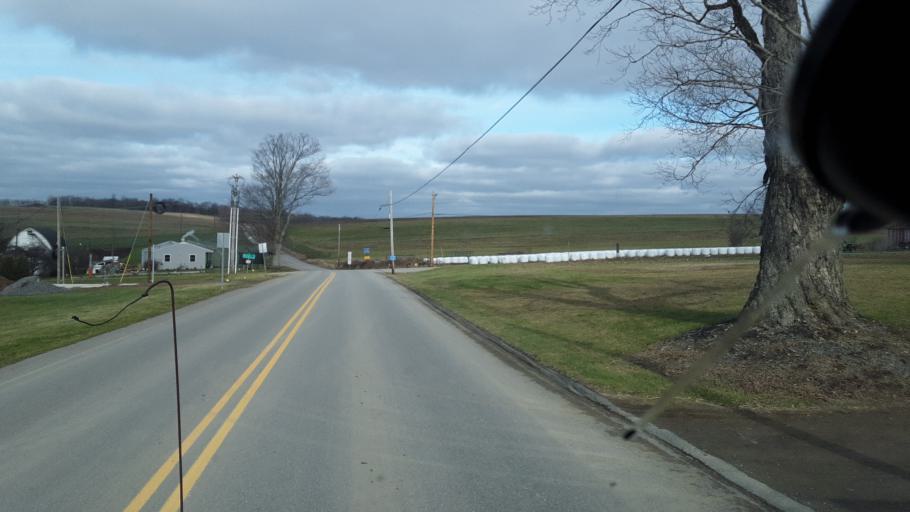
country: US
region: Pennsylvania
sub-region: Potter County
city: Galeton
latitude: 41.8858
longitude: -77.7613
